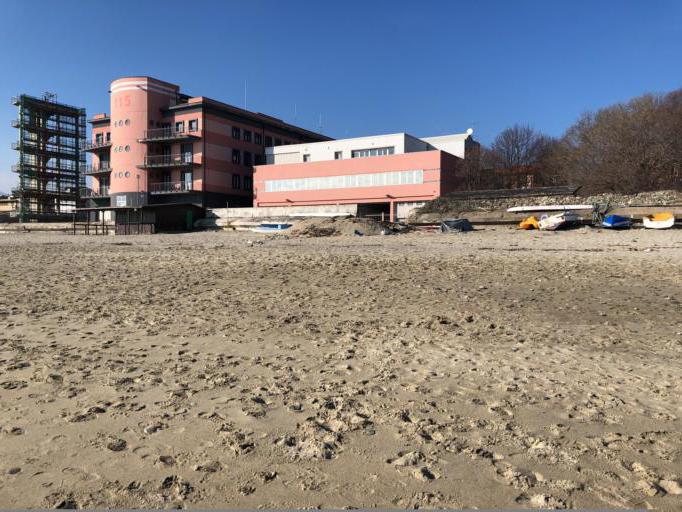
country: IT
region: Liguria
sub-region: Provincia di Savona
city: Savona
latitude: 44.2920
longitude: 8.4566
